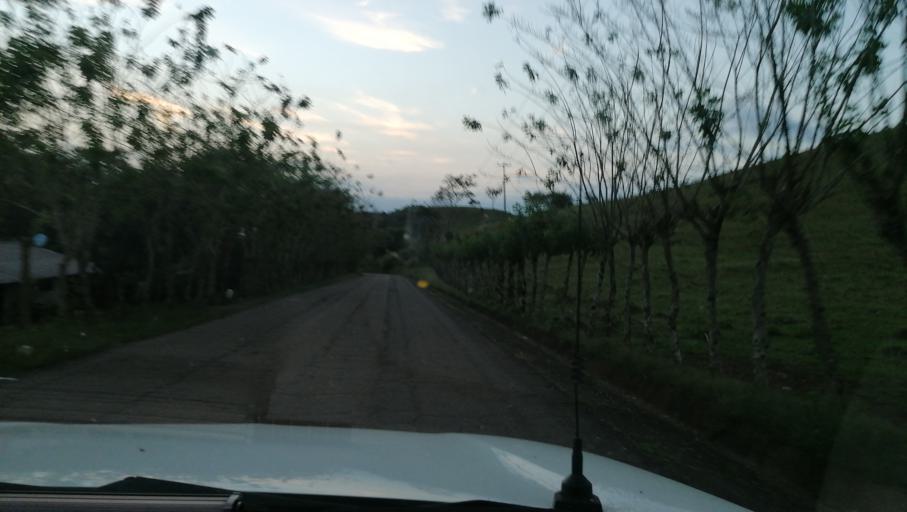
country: MX
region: Chiapas
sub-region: Ostuacan
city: Nuevo Juan del Grijalva
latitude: 17.4461
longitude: -93.3547
